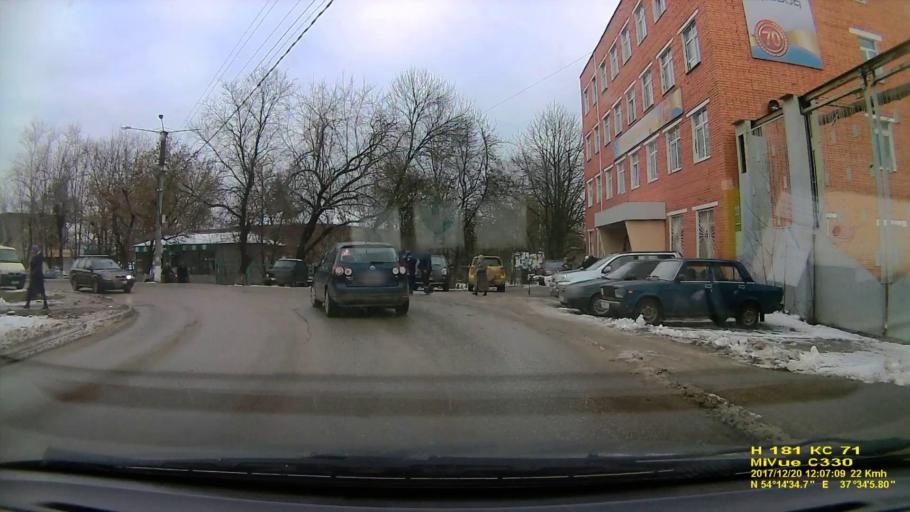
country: RU
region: Tula
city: Gorelki
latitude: 54.2430
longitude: 37.5685
